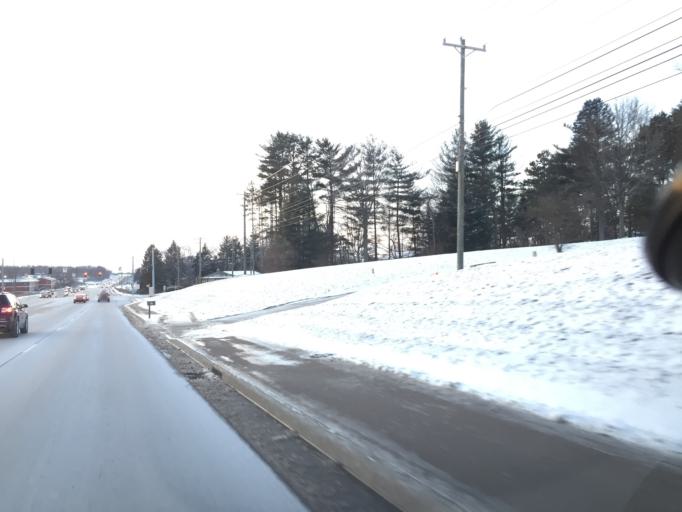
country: US
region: Indiana
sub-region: Monroe County
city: Bloomington
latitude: 39.1862
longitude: -86.5265
